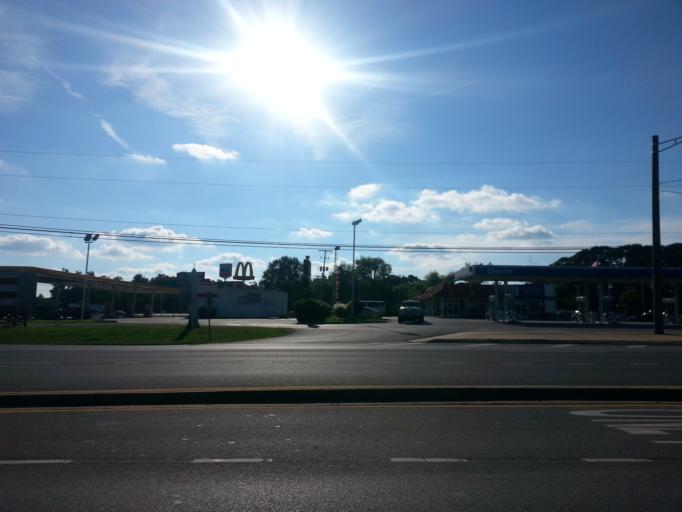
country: US
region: Alabama
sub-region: Colbert County
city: Muscle Shoals
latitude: 34.7125
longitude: -87.6677
